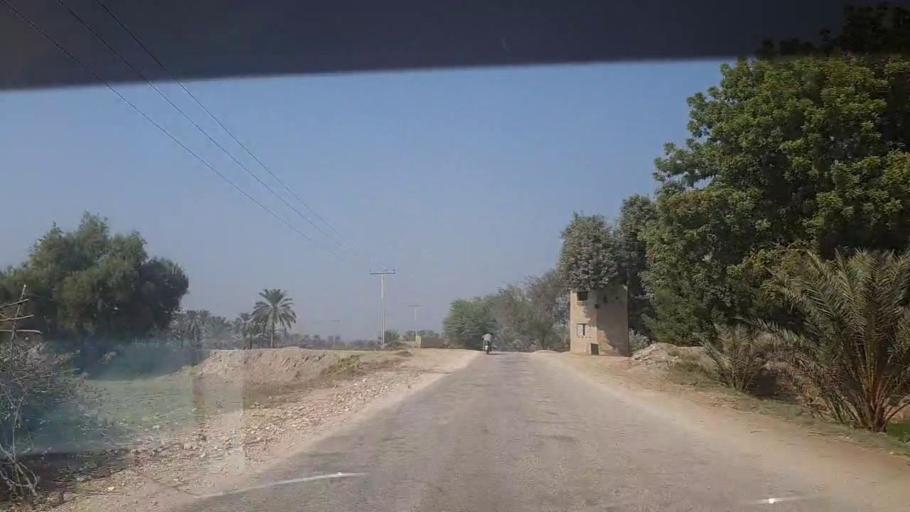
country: PK
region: Sindh
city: Kot Diji
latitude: 27.3704
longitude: 68.7005
